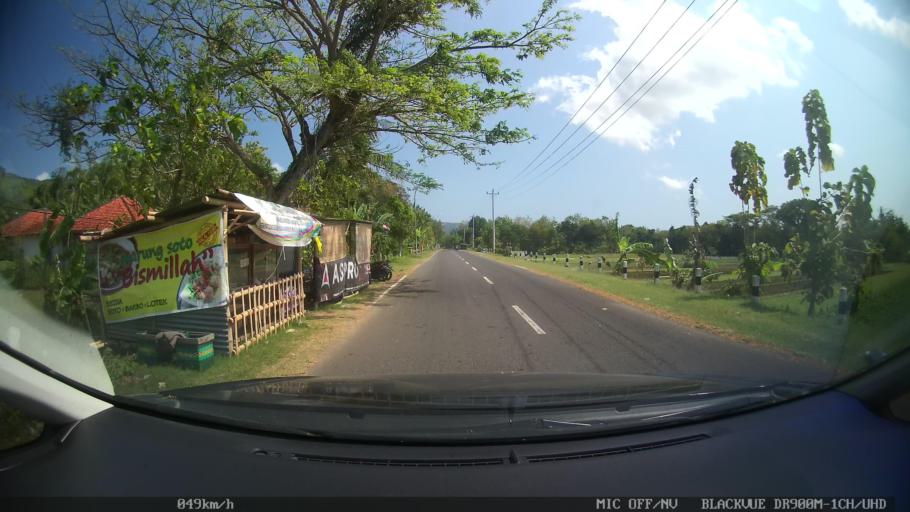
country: ID
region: Daerah Istimewa Yogyakarta
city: Pundong
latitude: -7.9606
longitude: 110.3574
